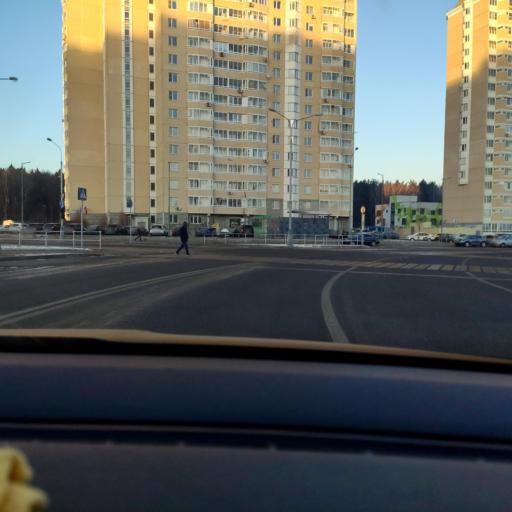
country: RU
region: Moscow
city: Novo-Peredelkino
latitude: 55.6381
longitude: 37.3091
